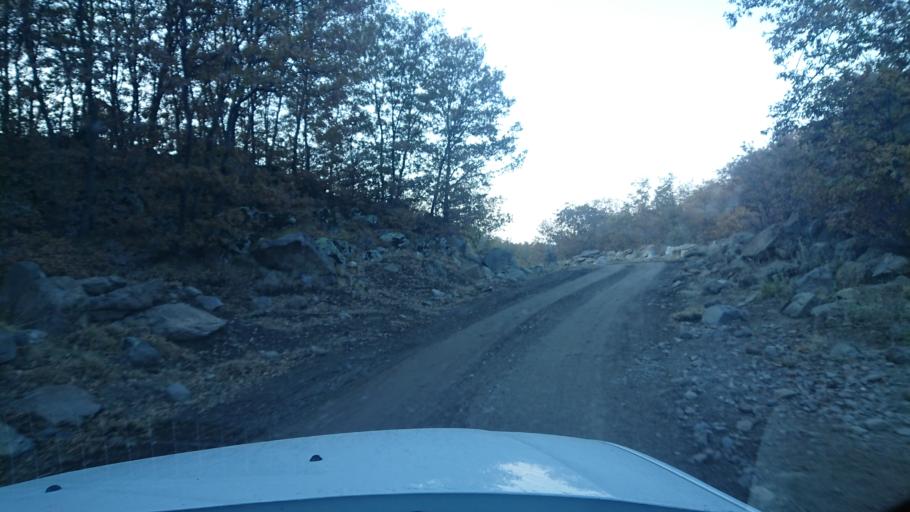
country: TR
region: Aksaray
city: Taspinar
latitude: 38.1648
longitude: 34.2085
